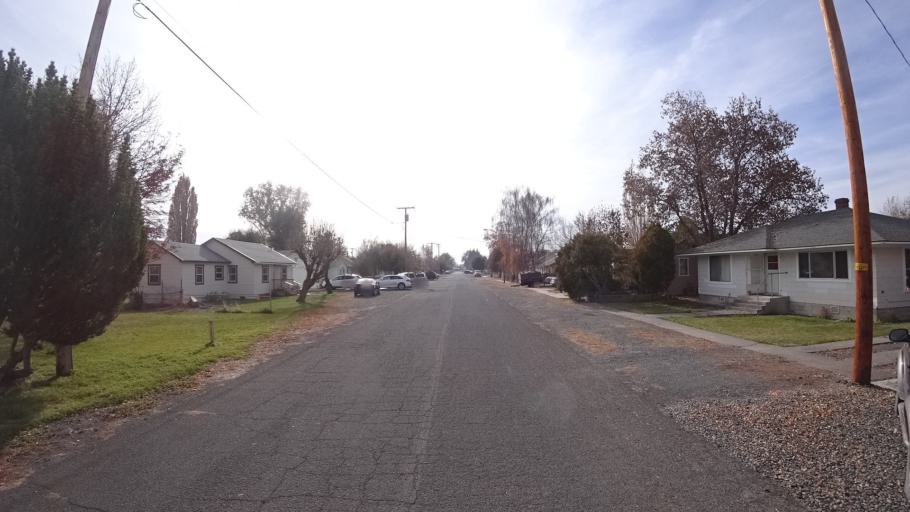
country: US
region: California
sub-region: Siskiyou County
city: Tulelake
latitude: 41.9598
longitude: -121.4792
